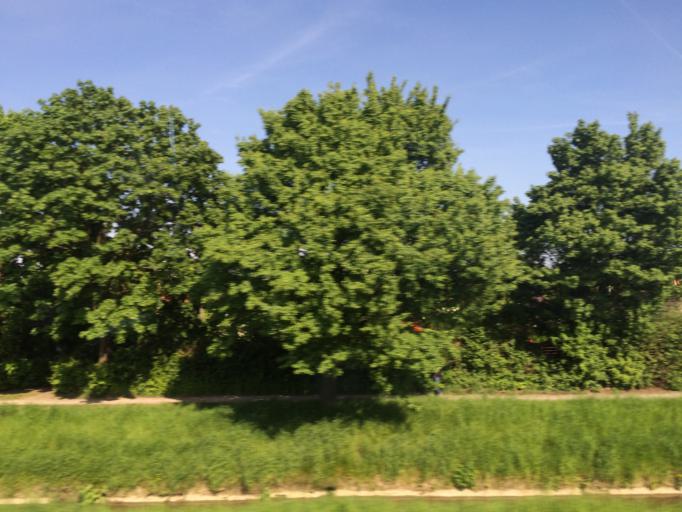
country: DE
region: North Rhine-Westphalia
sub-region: Regierungsbezirk Dusseldorf
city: Dusseldorf
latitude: 51.2573
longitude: 6.7928
